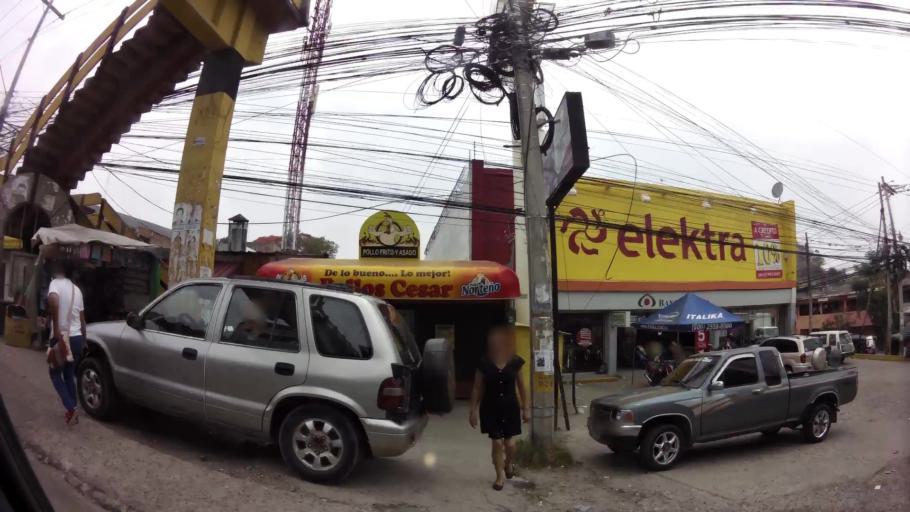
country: HN
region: Francisco Morazan
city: Tegucigalpa
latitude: 14.0650
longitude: -87.2087
